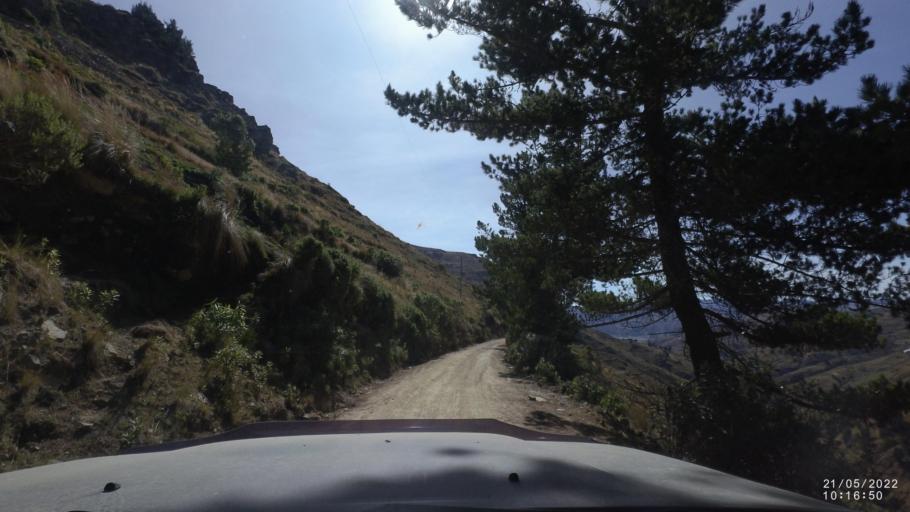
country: BO
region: Cochabamba
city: Colomi
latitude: -17.3313
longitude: -65.9661
